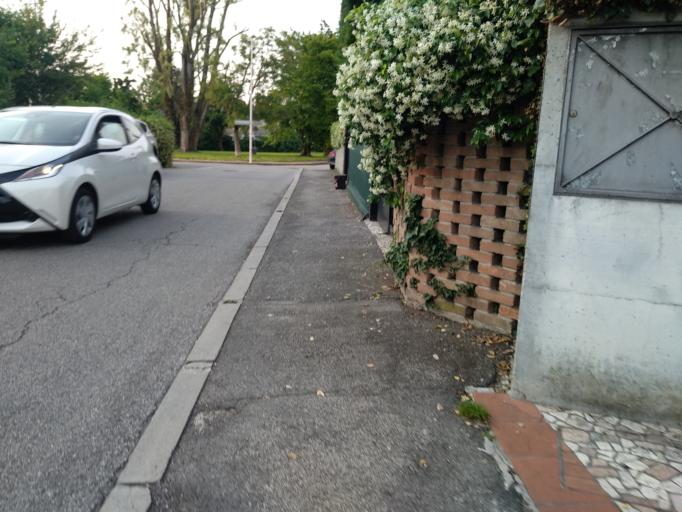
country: IT
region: Veneto
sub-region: Provincia di Padova
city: Mandriola-Sant'Agostino
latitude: 45.3795
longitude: 11.8503
